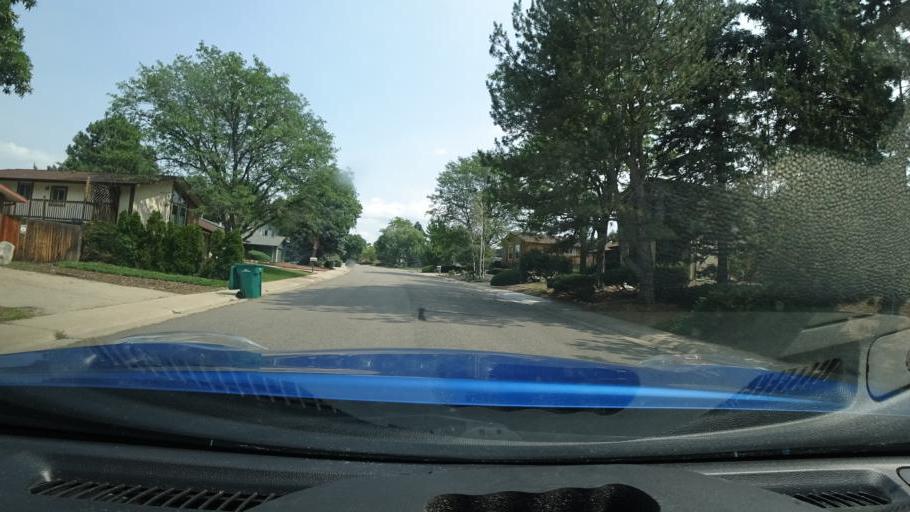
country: US
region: Colorado
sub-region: Adams County
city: Aurora
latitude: 39.6709
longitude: -104.8560
